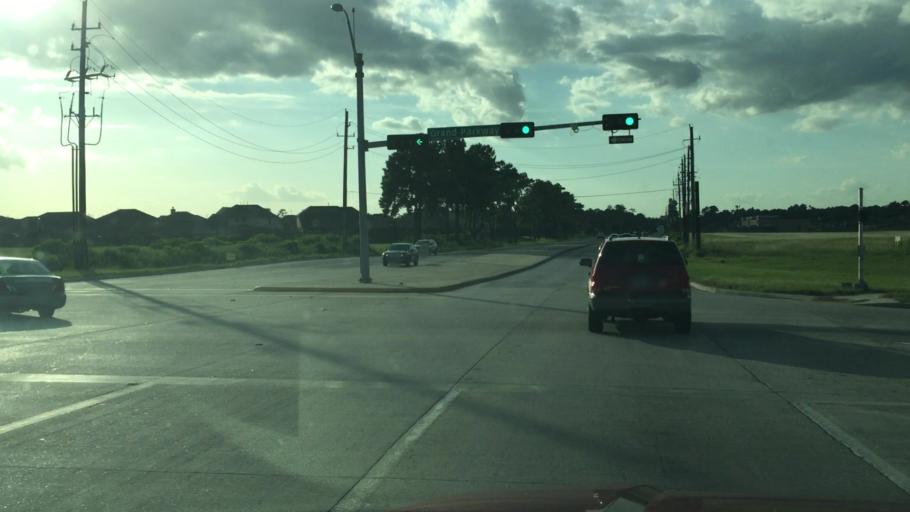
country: US
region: Texas
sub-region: Harris County
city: Tomball
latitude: 30.0757
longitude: -95.5571
